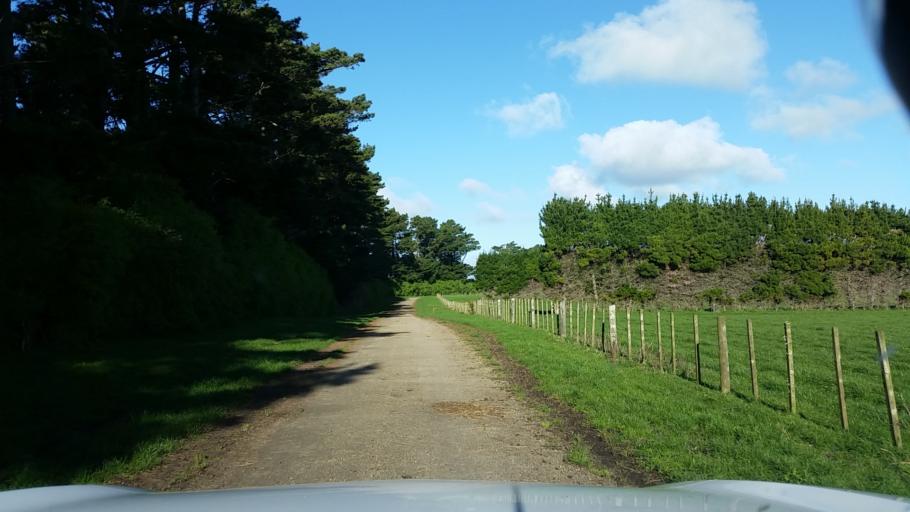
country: NZ
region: Taranaki
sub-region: South Taranaki District
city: Patea
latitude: -39.7388
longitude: 174.5422
